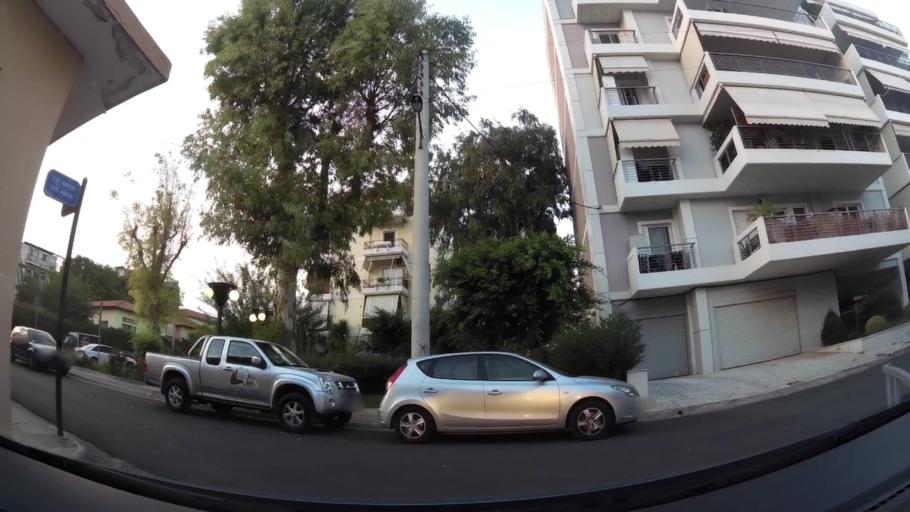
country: GR
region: Attica
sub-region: Nomarchia Athinas
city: Ilion
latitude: 38.0281
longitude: 23.6945
